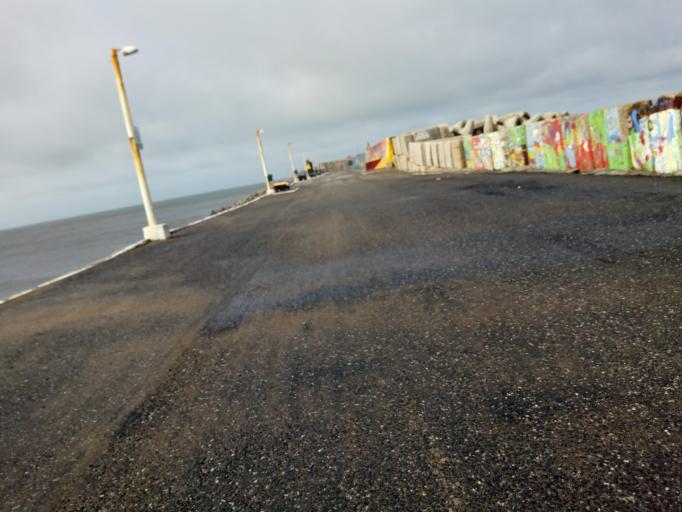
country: AR
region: Buenos Aires
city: Necochea
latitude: -38.5845
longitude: -58.6958
